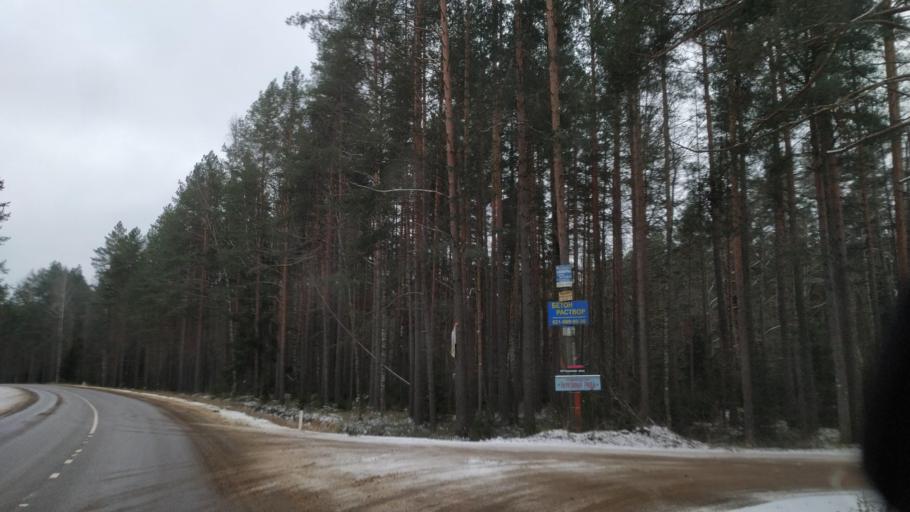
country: RU
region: Leningrad
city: Sosnovyy Bor
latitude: 59.8550
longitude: 29.1085
